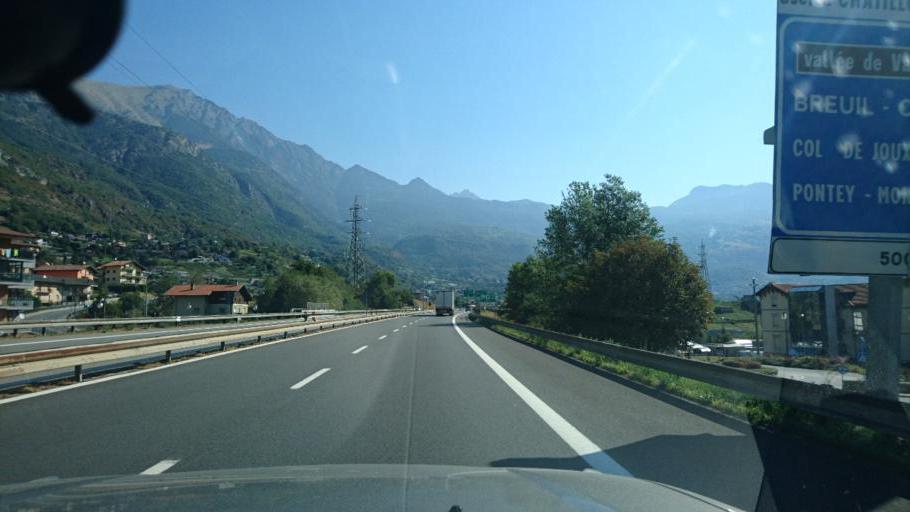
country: IT
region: Aosta Valley
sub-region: Valle d'Aosta
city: Chatillon
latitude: 45.7464
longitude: 7.6158
